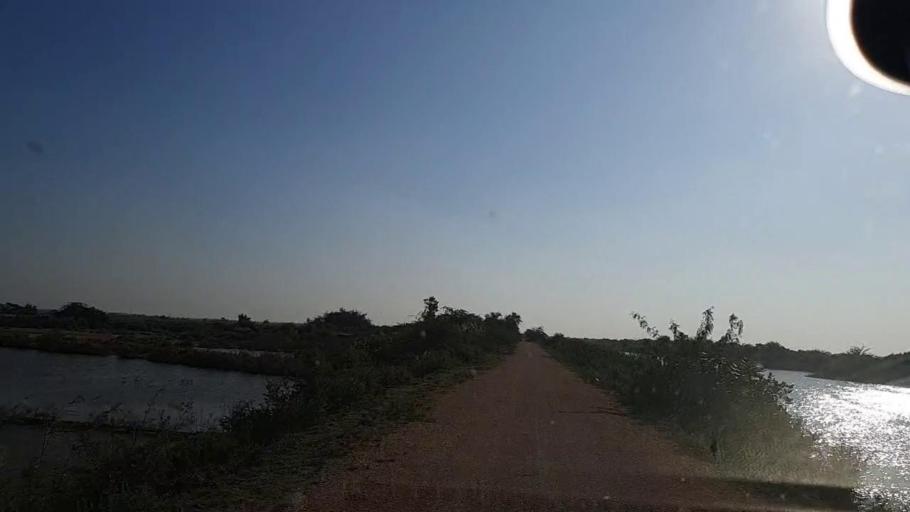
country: PK
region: Sindh
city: Chuhar Jamali
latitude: 24.5578
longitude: 68.0383
